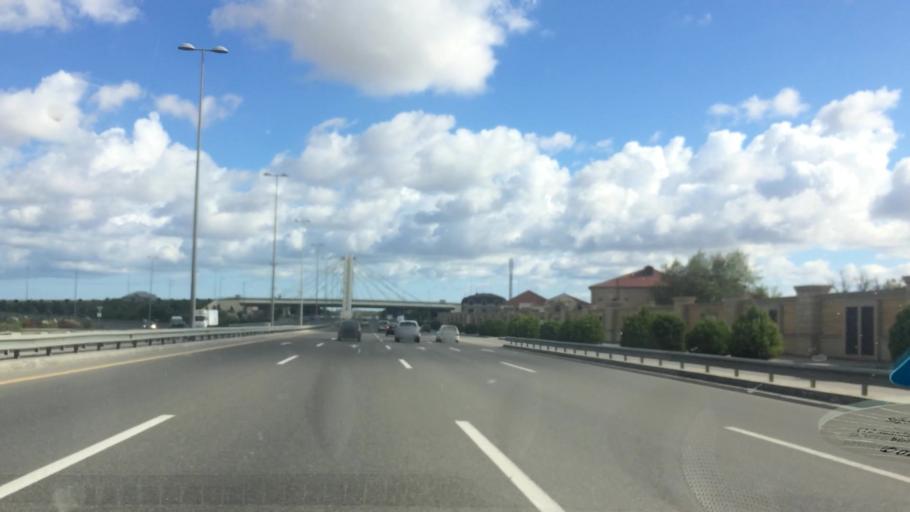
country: AZ
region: Baki
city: Biny Selo
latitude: 40.4573
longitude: 50.0719
